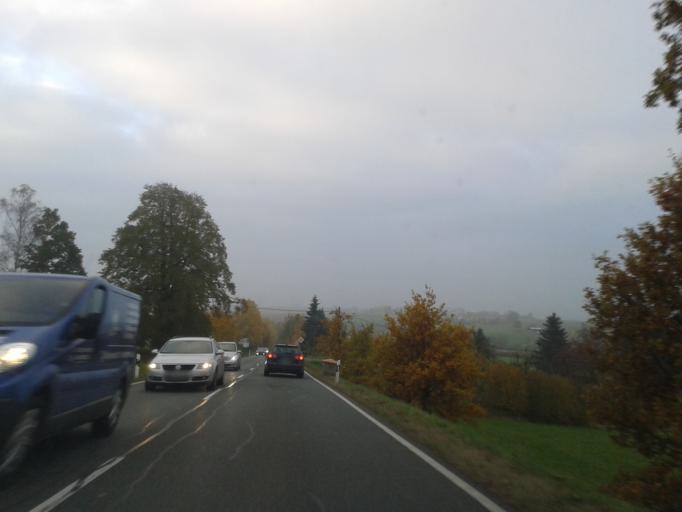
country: DE
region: Saxony
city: Niederschona
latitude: 50.9667
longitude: 13.4249
